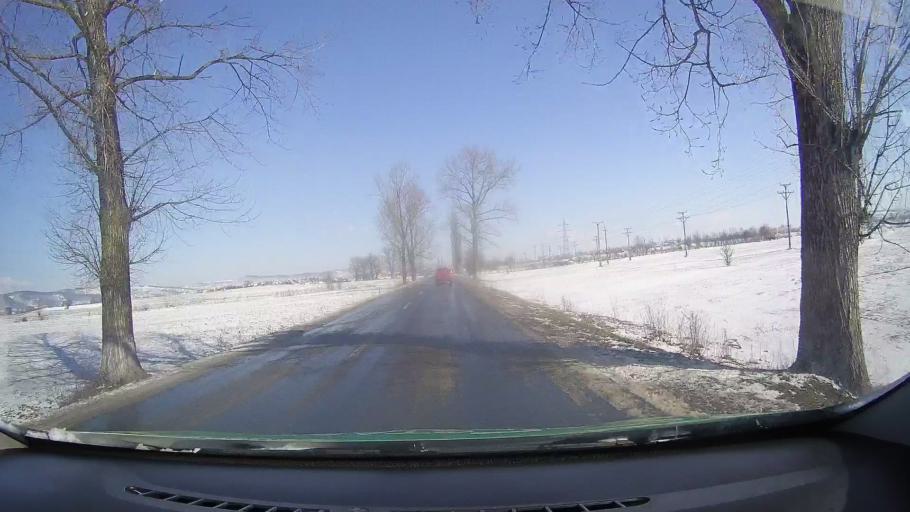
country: RO
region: Sibiu
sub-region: Comuna Avrig
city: Avrig
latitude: 45.7137
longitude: 24.3708
